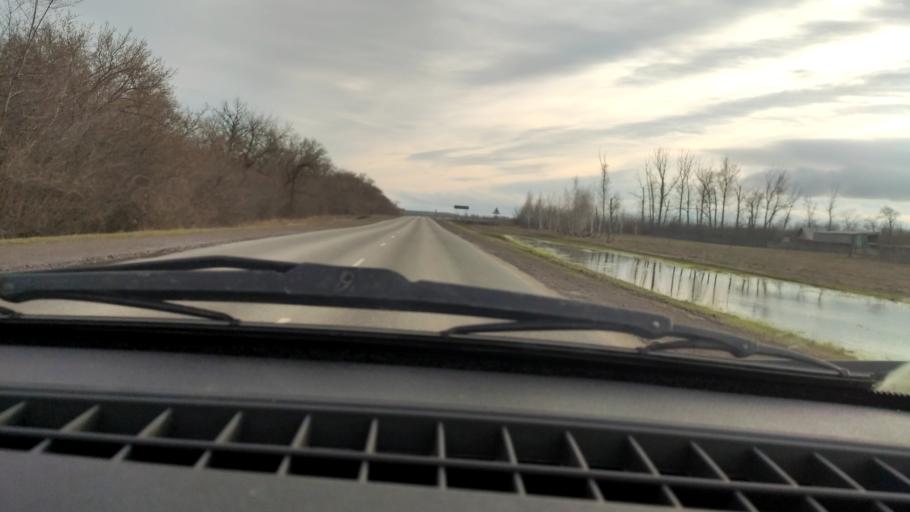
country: RU
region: Bashkortostan
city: Davlekanovo
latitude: 54.2893
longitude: 55.1188
